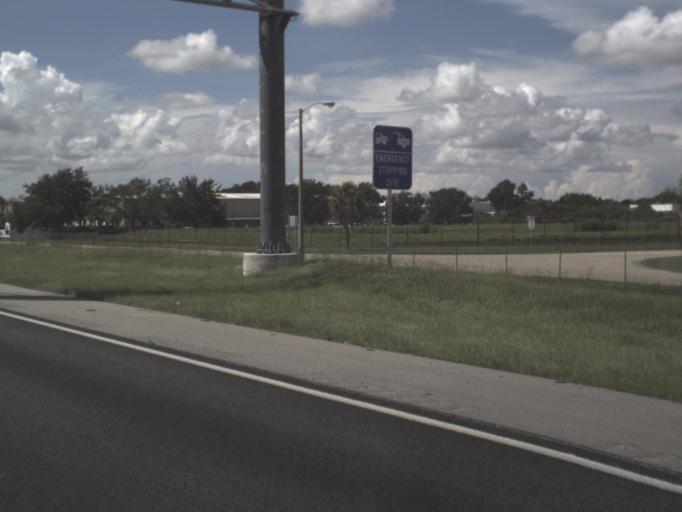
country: US
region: Florida
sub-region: Lee County
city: Tice
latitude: 26.6685
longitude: -81.7999
